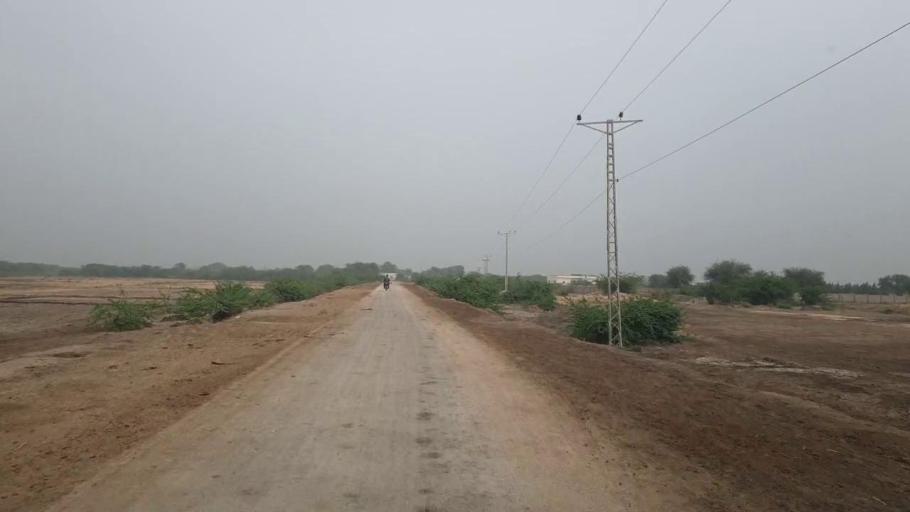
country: PK
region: Sindh
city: Badin
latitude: 24.5722
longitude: 68.6664
